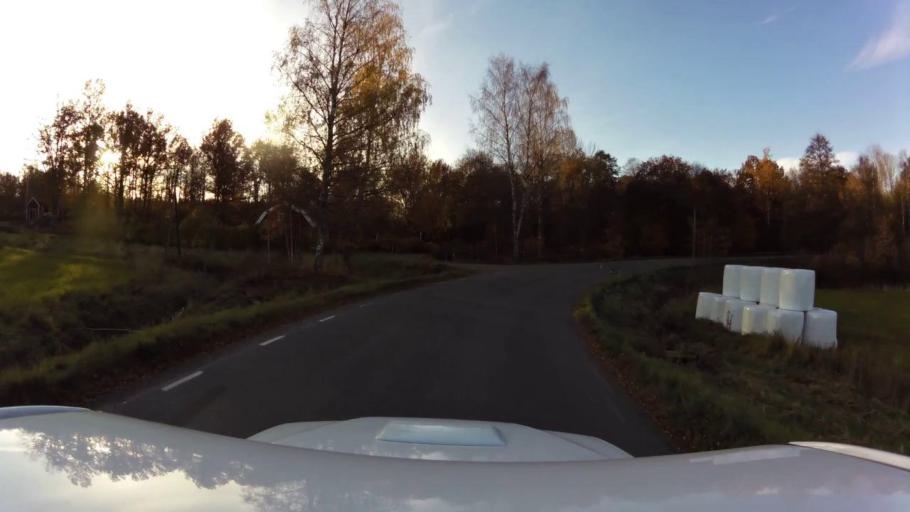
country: SE
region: OEstergoetland
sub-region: Linkopings Kommun
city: Sturefors
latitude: 58.2463
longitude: 15.6634
